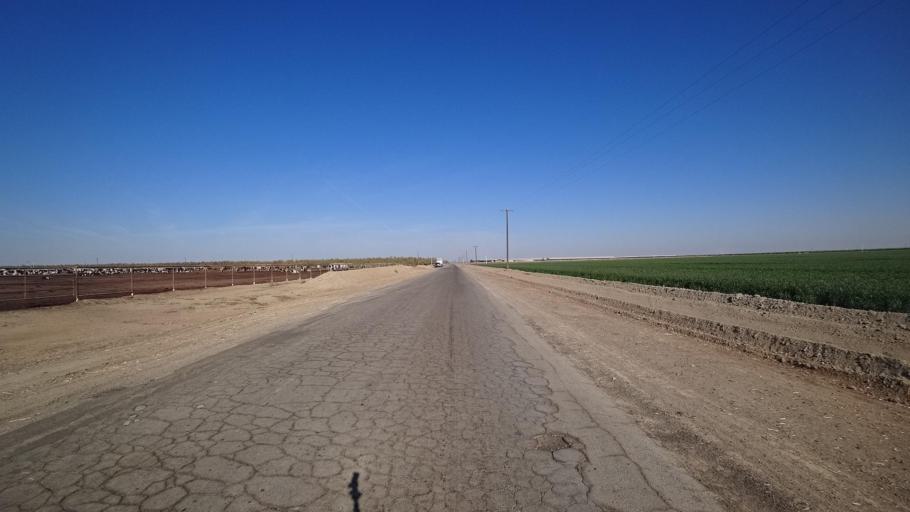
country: US
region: California
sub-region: Kern County
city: Wasco
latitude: 35.7260
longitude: -119.4193
